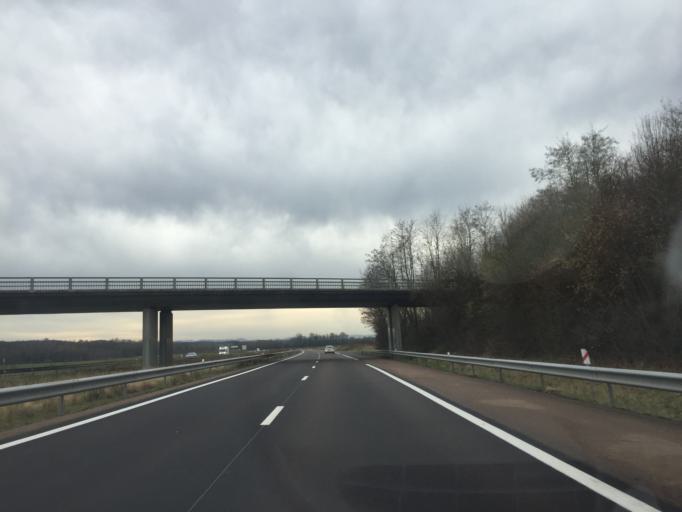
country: FR
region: Franche-Comte
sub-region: Departement du Jura
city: Bletterans
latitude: 46.7596
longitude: 5.5094
